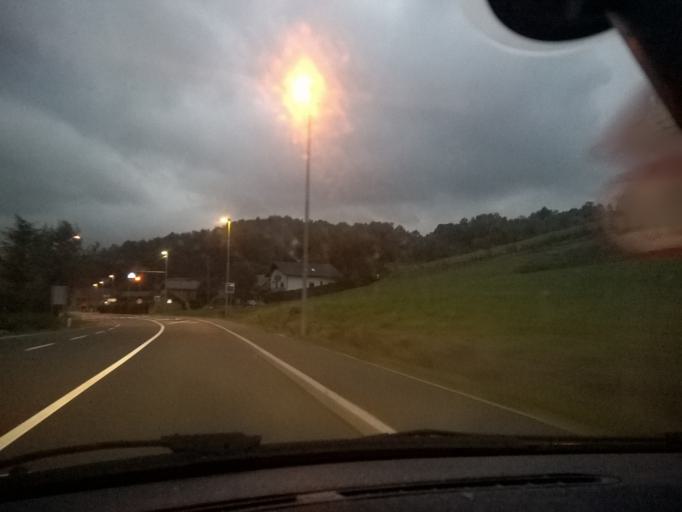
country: HR
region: Krapinsko-Zagorska
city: Pregrada
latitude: 46.2094
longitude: 15.7613
